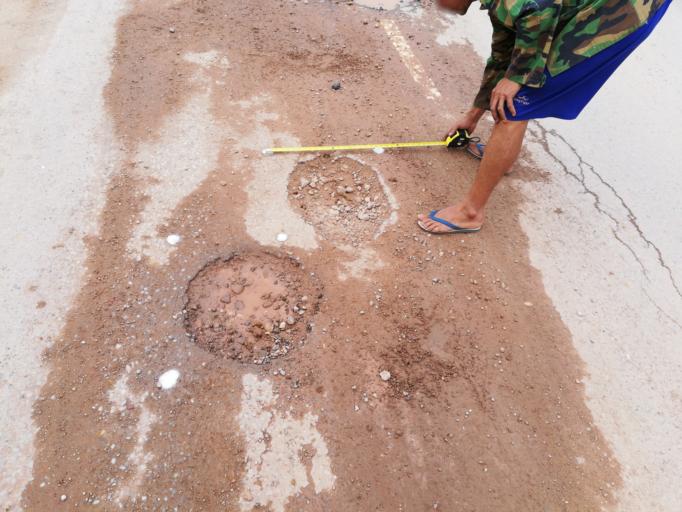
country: LA
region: Loungnamtha
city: Louang Namtha
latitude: 20.9916
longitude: 101.4107
